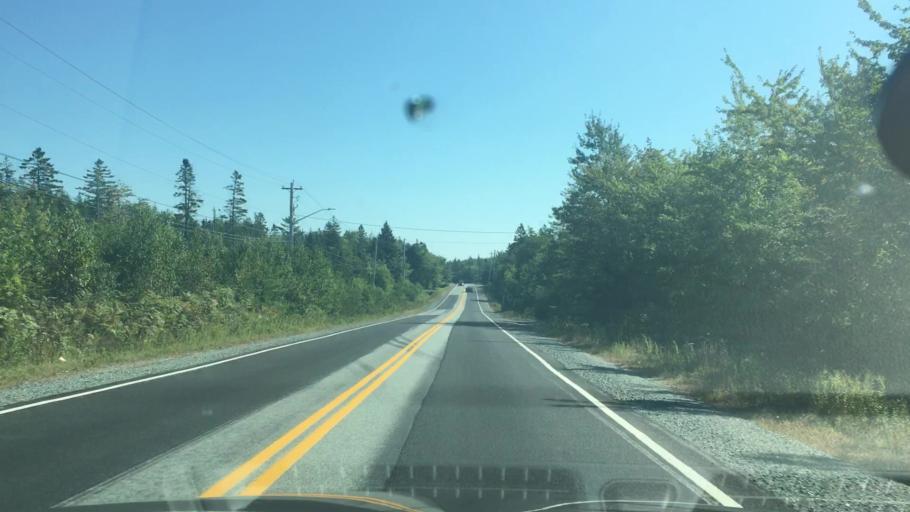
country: CA
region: Nova Scotia
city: New Glasgow
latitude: 44.9103
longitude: -62.5500
